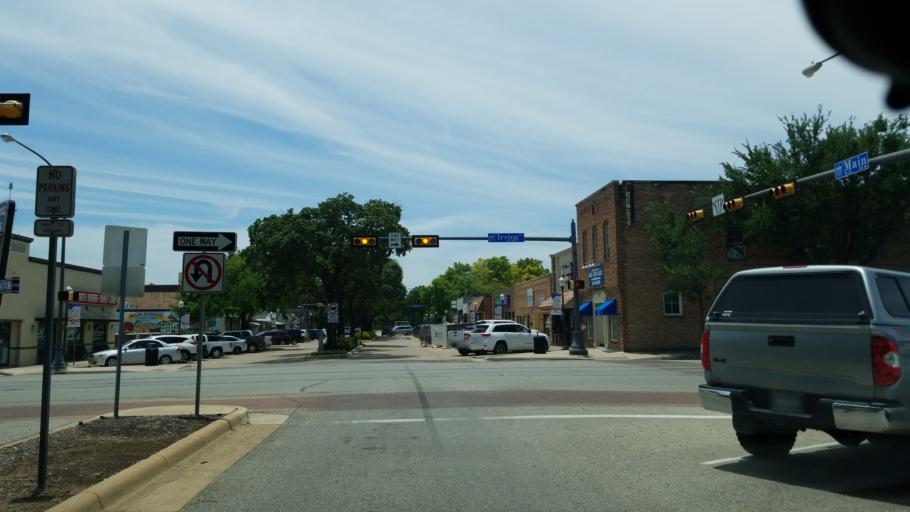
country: US
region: Texas
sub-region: Dallas County
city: Irving
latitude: 32.8141
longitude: -96.9462
